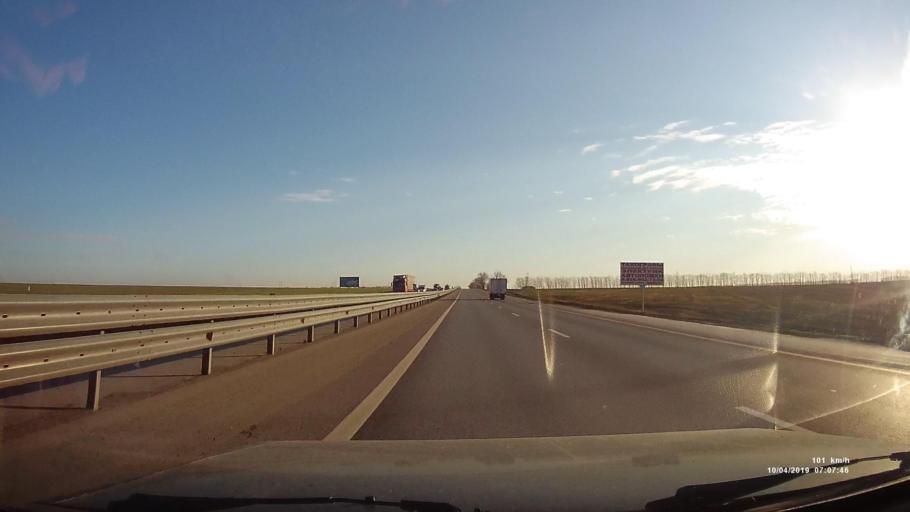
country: RU
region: Rostov
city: Mayskiy
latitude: 47.6675
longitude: 40.0553
